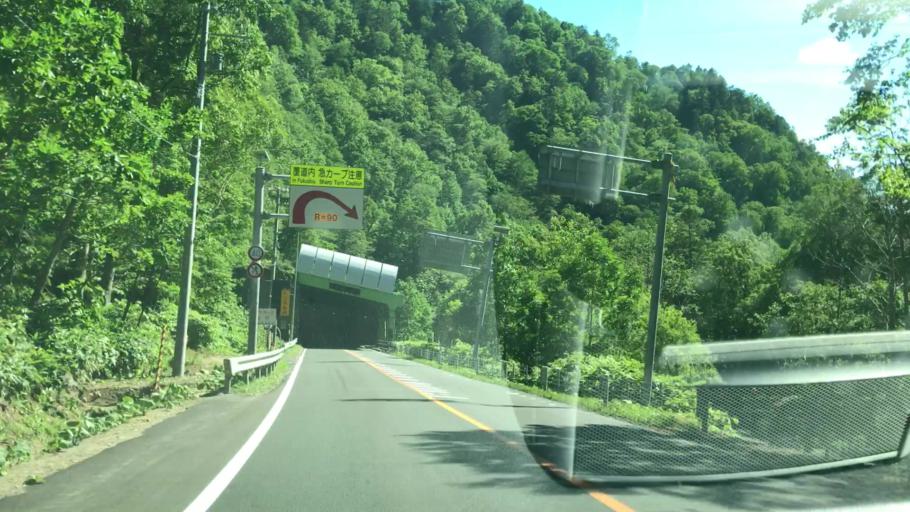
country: JP
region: Hokkaido
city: Shimo-furano
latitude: 42.9647
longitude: 142.6233
